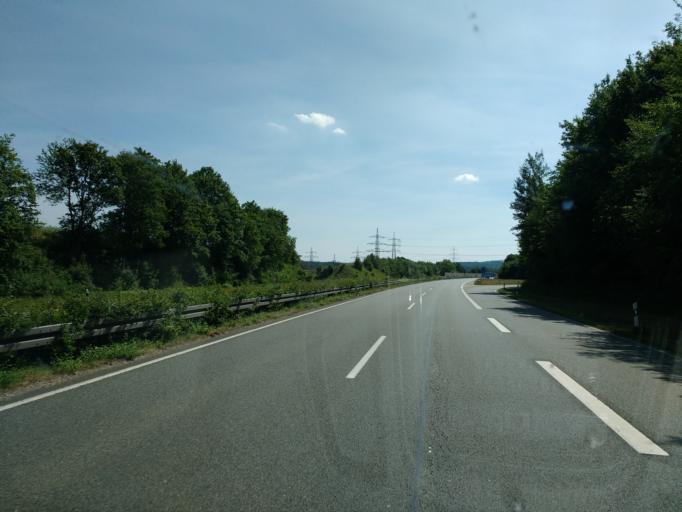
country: DE
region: Lower Saxony
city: Belm
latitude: 52.2712
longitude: 8.1043
